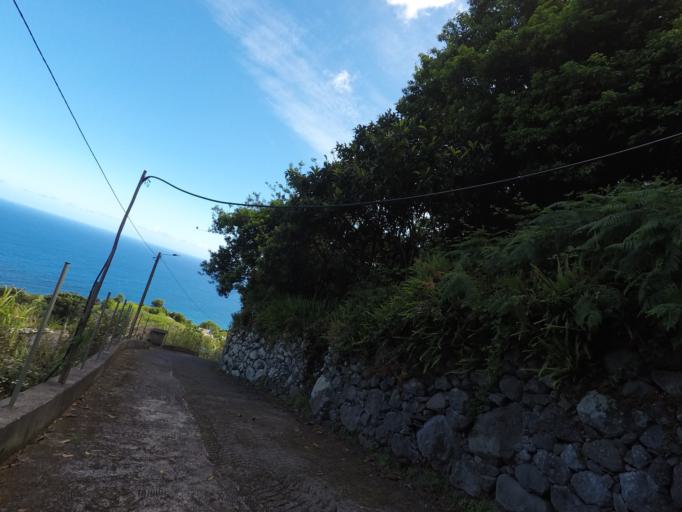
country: PT
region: Madeira
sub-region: Santana
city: Santana
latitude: 32.8234
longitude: -16.9495
